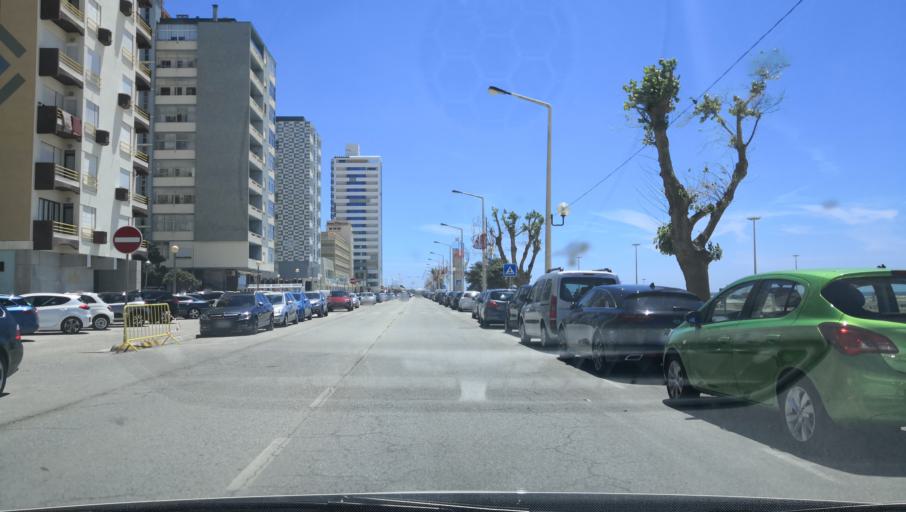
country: PT
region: Coimbra
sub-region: Figueira da Foz
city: Figueira da Foz
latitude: 40.1534
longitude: -8.8670
